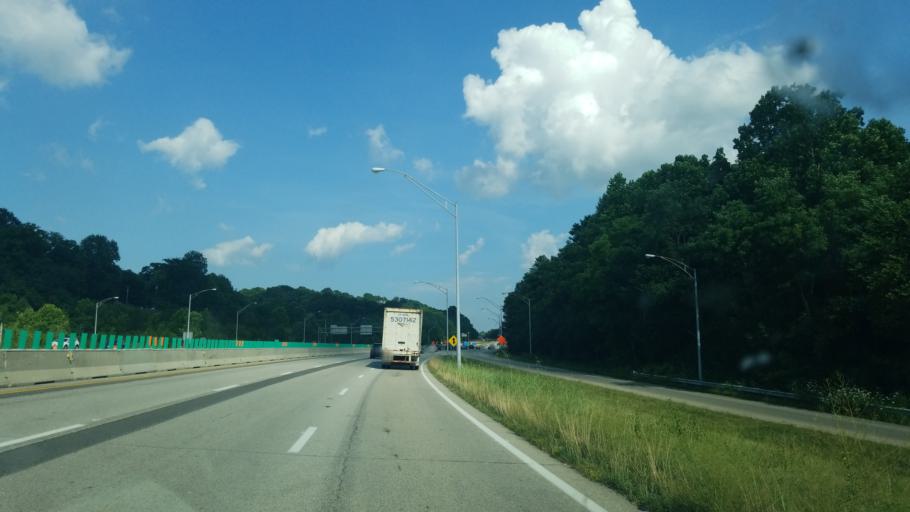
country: US
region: Kentucky
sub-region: Campbell County
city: Fort Thomas
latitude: 39.0602
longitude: -84.4186
